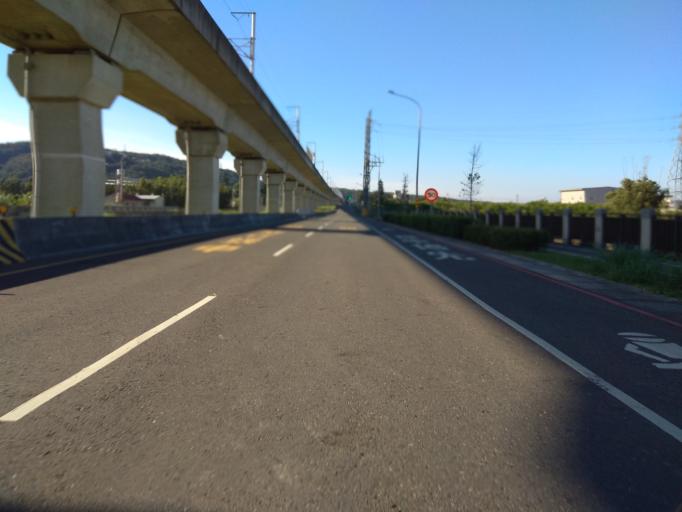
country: TW
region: Taiwan
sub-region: Hsinchu
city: Zhubei
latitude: 24.8884
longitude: 121.0735
